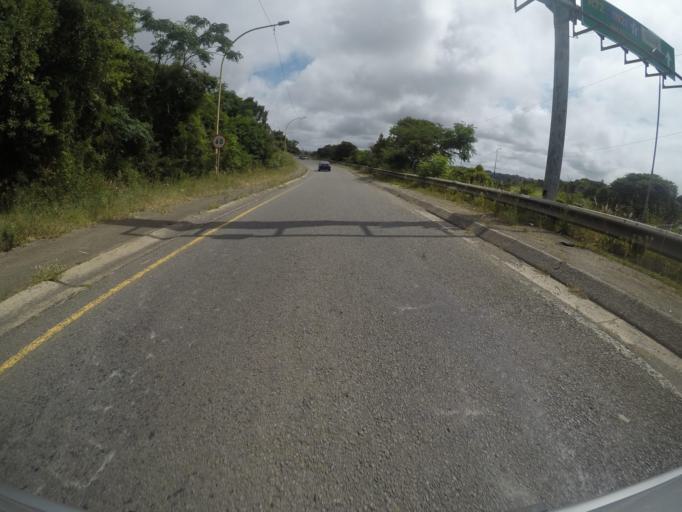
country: ZA
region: Eastern Cape
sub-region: Buffalo City Metropolitan Municipality
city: East London
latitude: -32.9805
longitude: 27.9194
